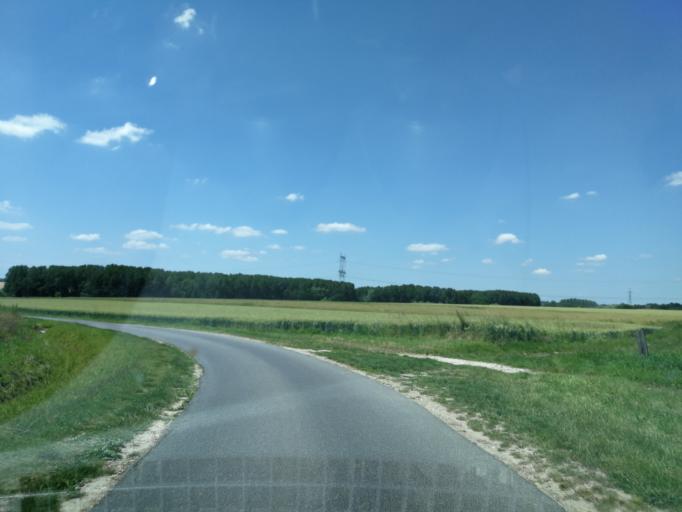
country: FR
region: Ile-de-France
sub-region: Departement de l'Essonne
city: Vaugrigneuse
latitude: 48.6060
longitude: 2.1281
